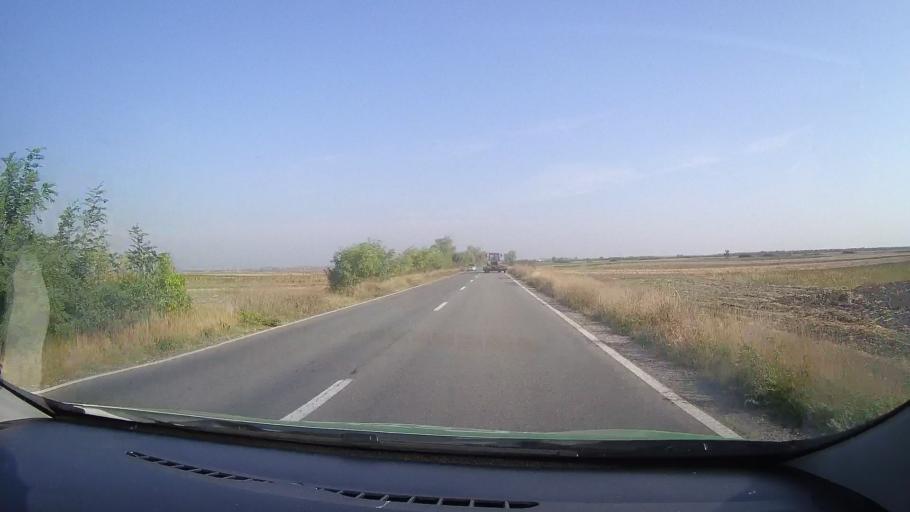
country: RO
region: Arad
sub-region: Comuna Pilu
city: Pilu
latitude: 46.5926
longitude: 21.3470
